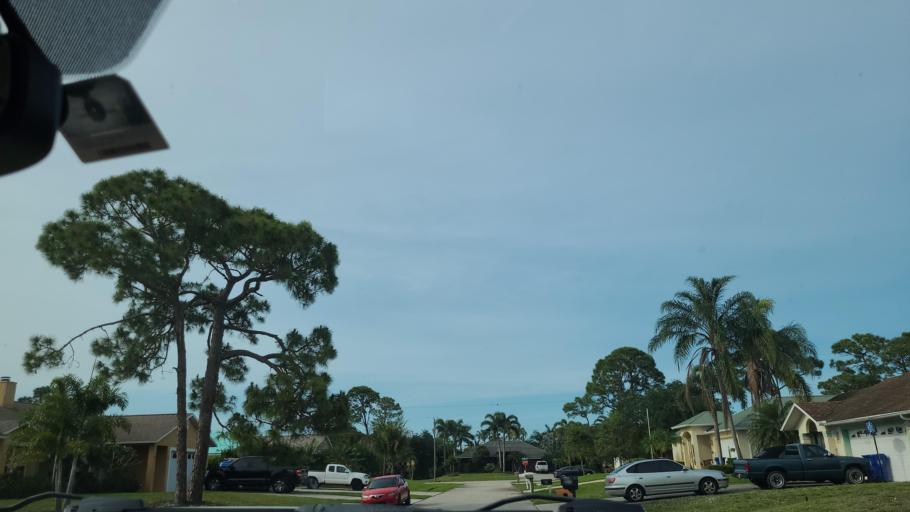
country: US
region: Florida
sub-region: Indian River County
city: Sebastian
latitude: 27.8029
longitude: -80.4707
